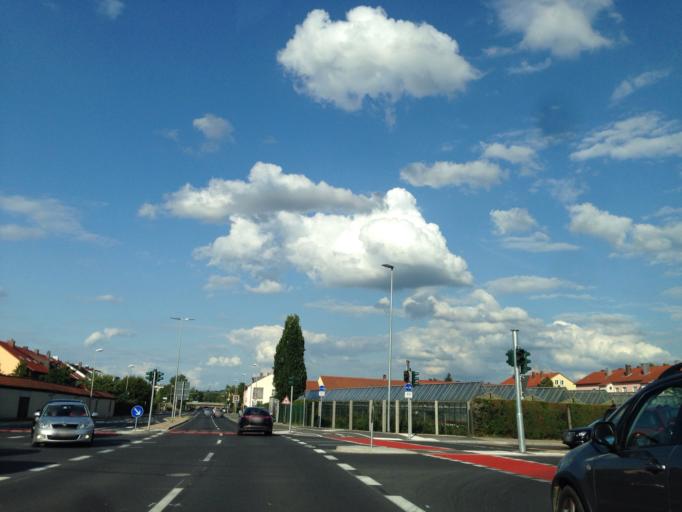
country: DE
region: Bavaria
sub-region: Upper Franconia
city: Bamberg
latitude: 49.8834
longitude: 10.9123
